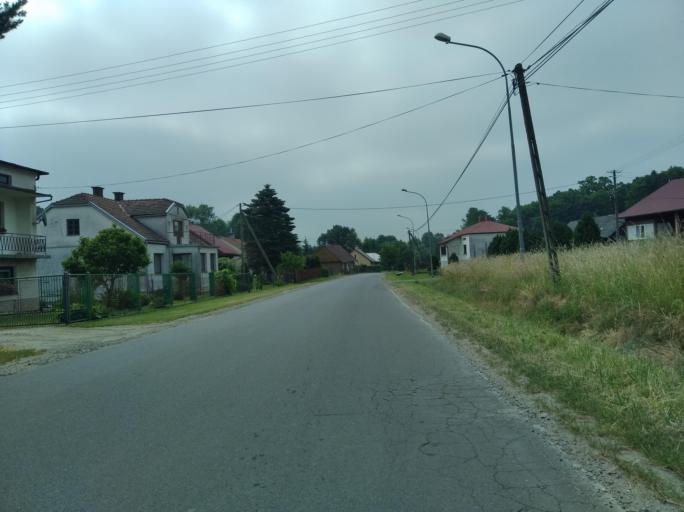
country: PL
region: Subcarpathian Voivodeship
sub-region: Powiat brzozowski
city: Haczow
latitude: 49.6592
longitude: 21.9010
